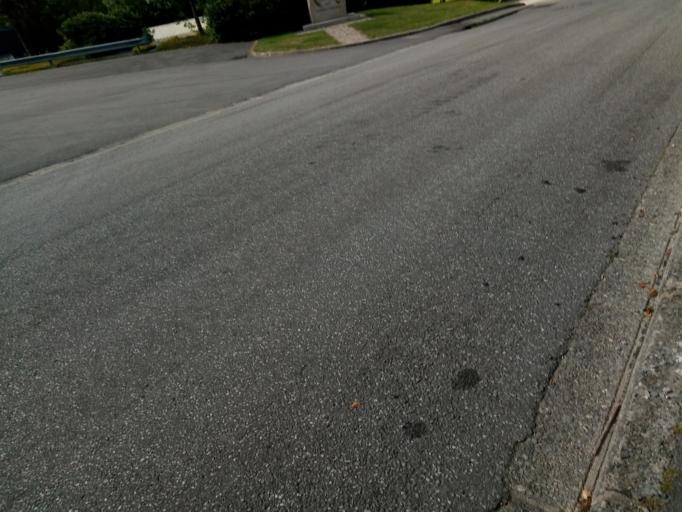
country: FR
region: Brittany
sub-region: Departement du Morbihan
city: Gourin
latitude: 48.1402
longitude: -3.6111
